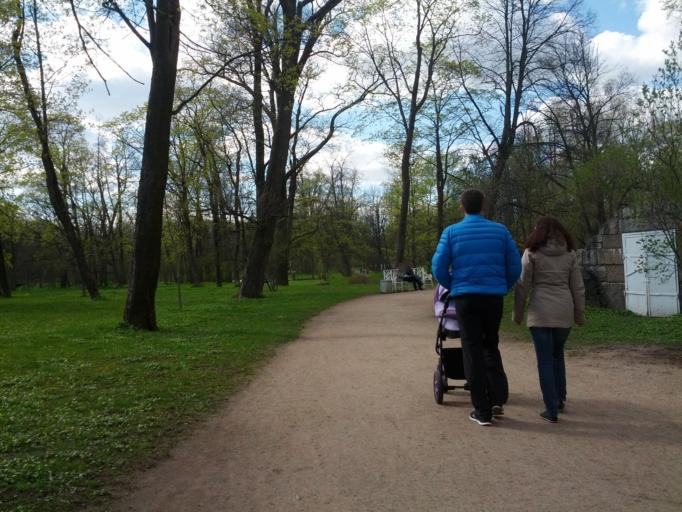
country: RU
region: St.-Petersburg
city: Pushkin
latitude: 59.7182
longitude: 30.3953
